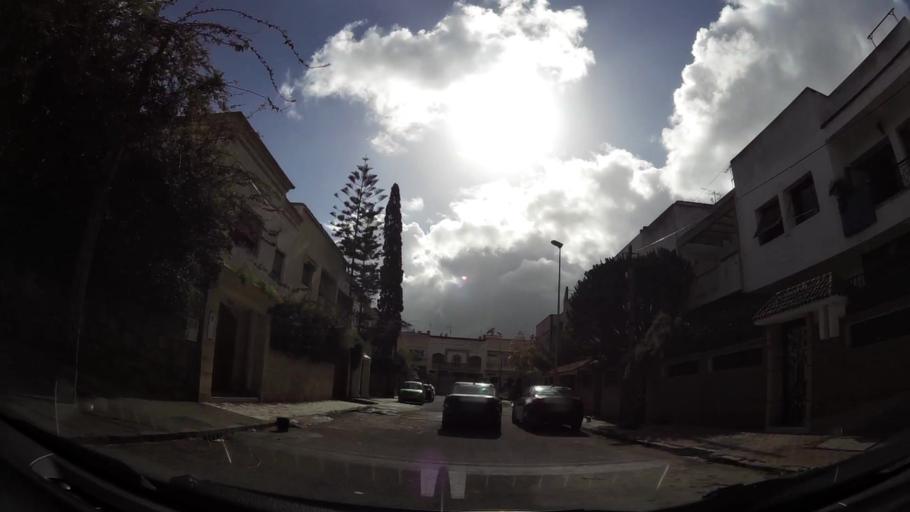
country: MA
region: Grand Casablanca
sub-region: Casablanca
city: Casablanca
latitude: 33.5466
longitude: -7.6037
